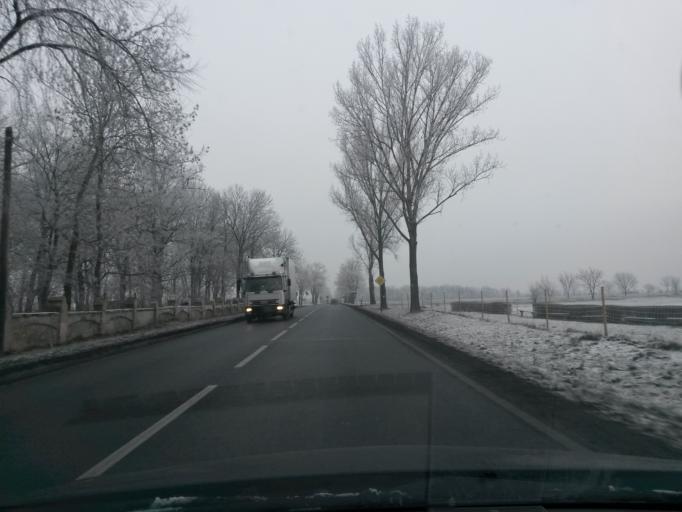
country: PL
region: Kujawsko-Pomorskie
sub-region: Powiat mogilenski
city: Strzelno
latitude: 52.7099
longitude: 18.2190
